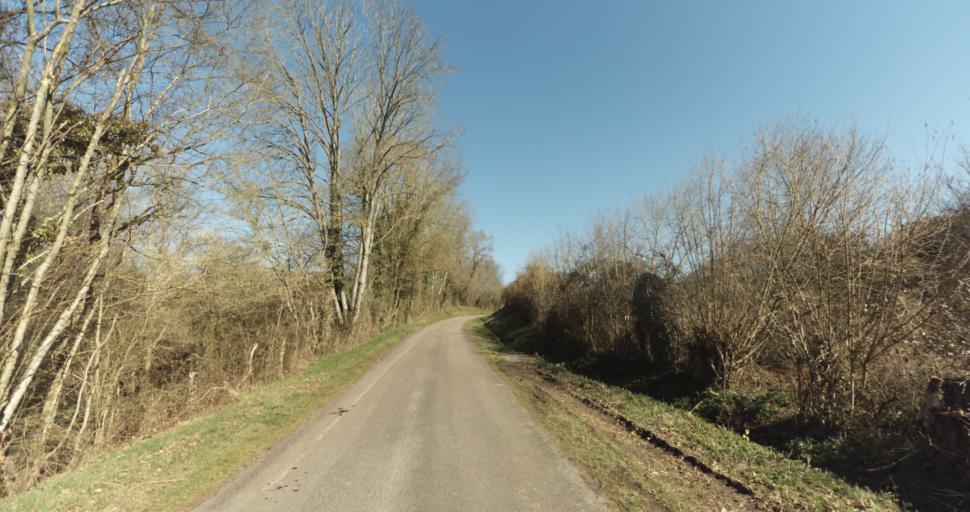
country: FR
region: Lower Normandy
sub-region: Departement du Calvados
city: Livarot
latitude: 48.9823
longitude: 0.0602
